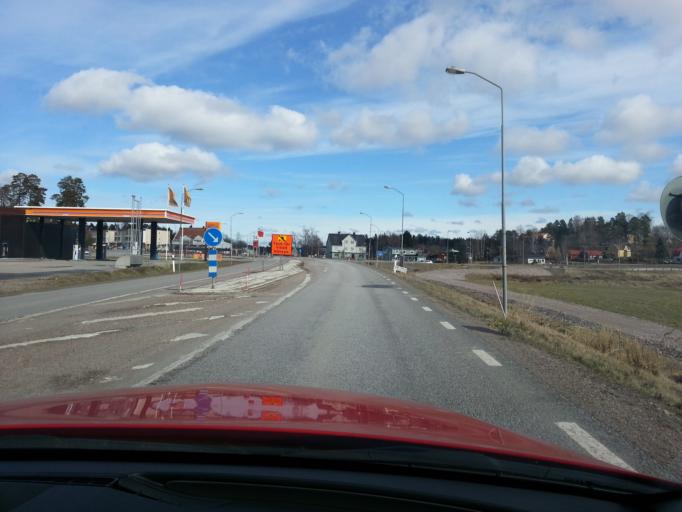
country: SE
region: Uppsala
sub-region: Osthammars Kommun
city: Gimo
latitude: 60.0616
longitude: 18.0780
